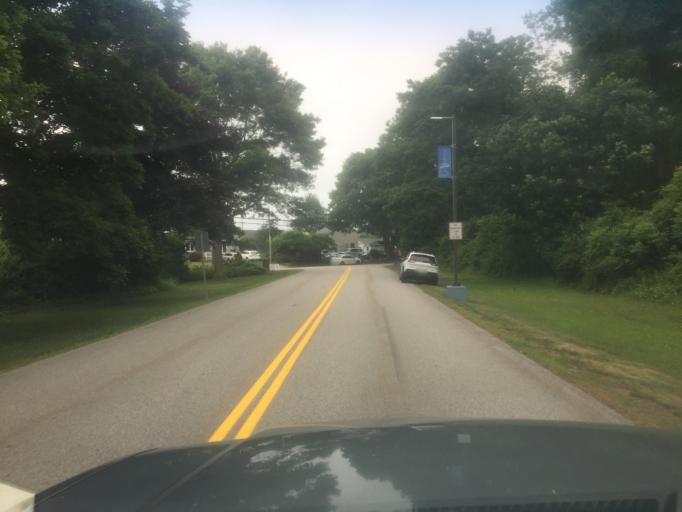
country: US
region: Maine
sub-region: York County
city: York Harbor
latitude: 43.1525
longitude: -70.6282
